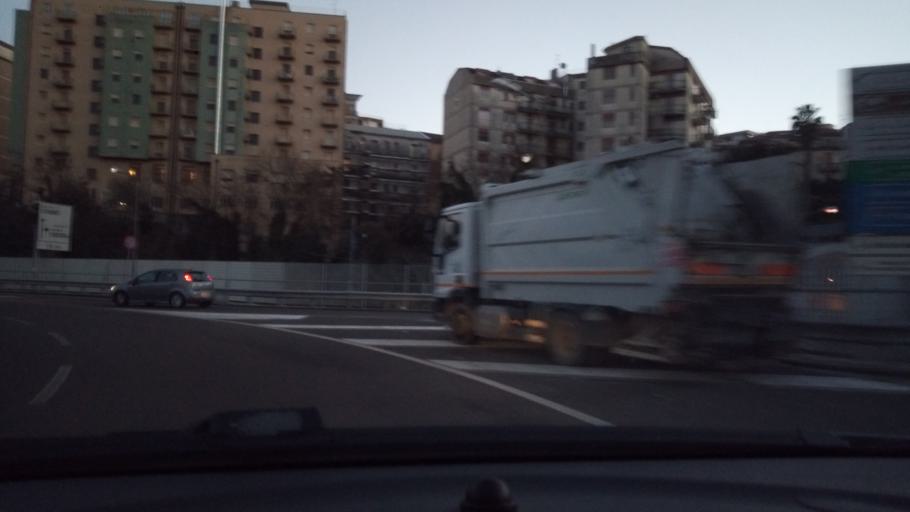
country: IT
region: Calabria
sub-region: Provincia di Catanzaro
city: Siano
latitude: 38.9114
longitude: 16.5907
